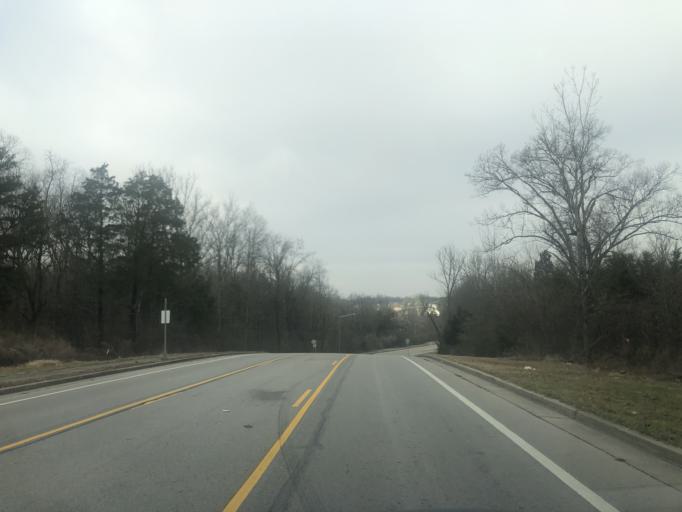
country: US
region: Tennessee
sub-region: Rutherford County
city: La Vergne
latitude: 36.0714
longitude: -86.6459
